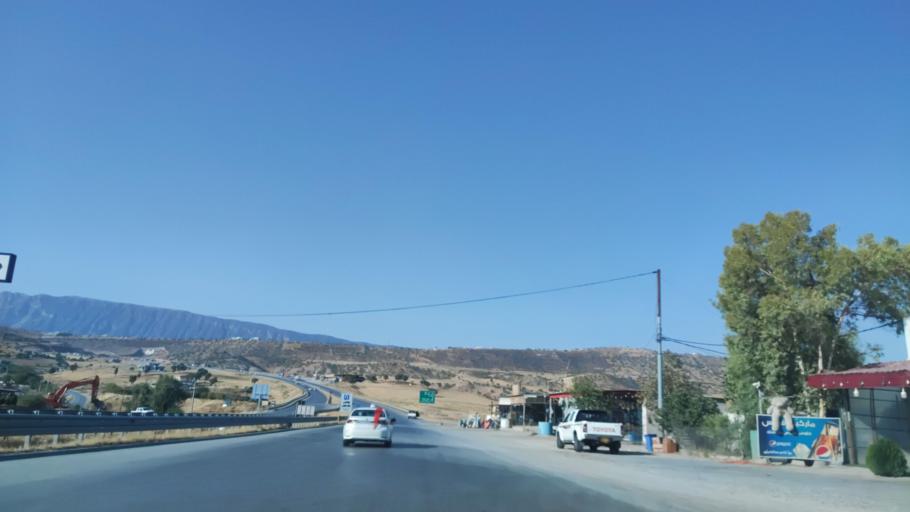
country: IQ
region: Arbil
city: Shaqlawah
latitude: 36.4539
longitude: 44.3813
